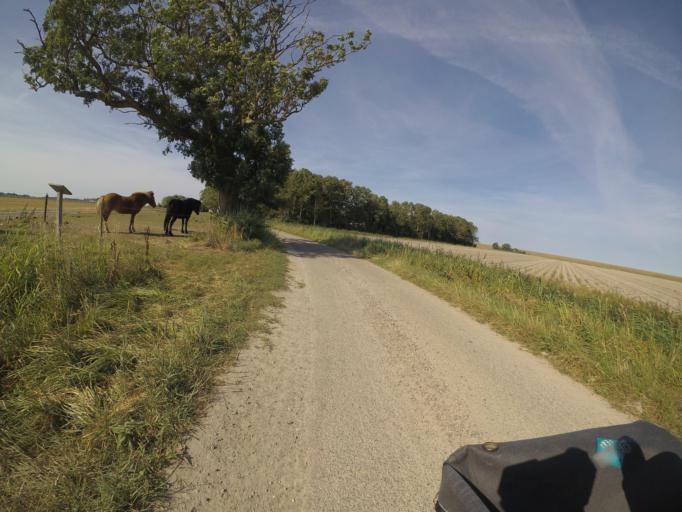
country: NL
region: Friesland
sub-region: Gemeente Ferwerderadiel
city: Ferwert
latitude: 53.3423
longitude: 5.8090
